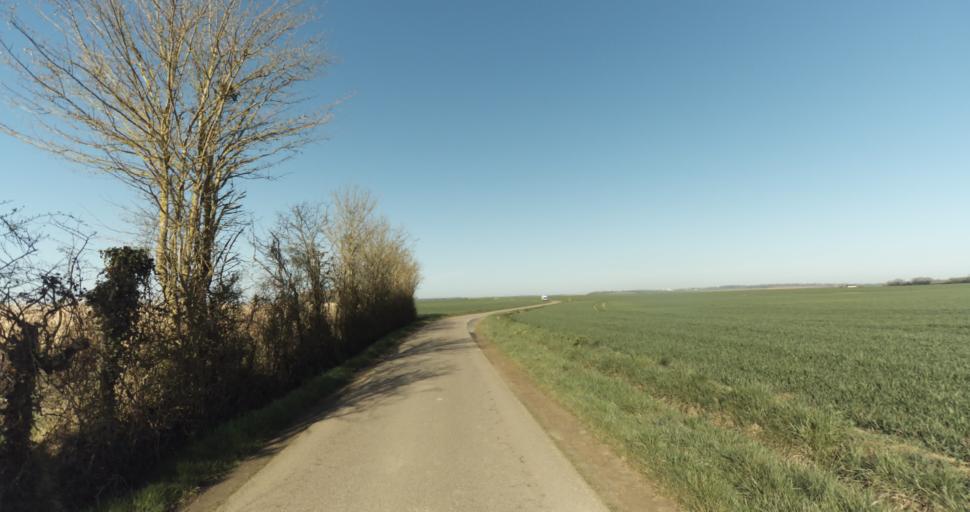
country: FR
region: Lower Normandy
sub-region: Departement du Calvados
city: Saint-Pierre-sur-Dives
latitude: 48.9903
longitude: -0.0302
